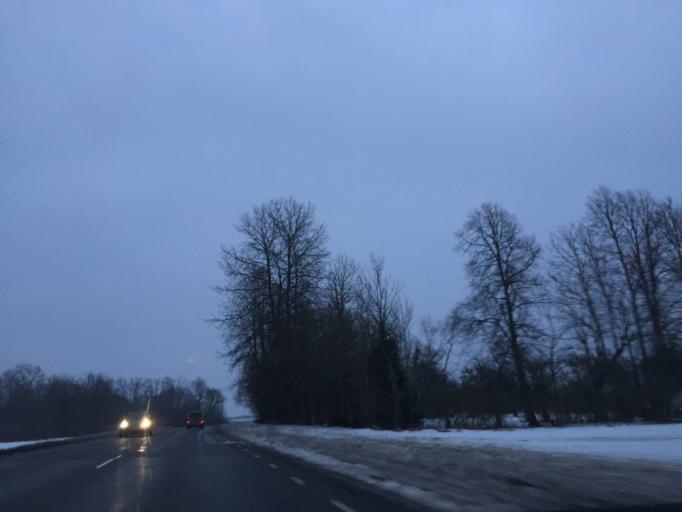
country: EE
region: Paernumaa
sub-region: Audru vald
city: Audru
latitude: 58.5072
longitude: 24.1107
